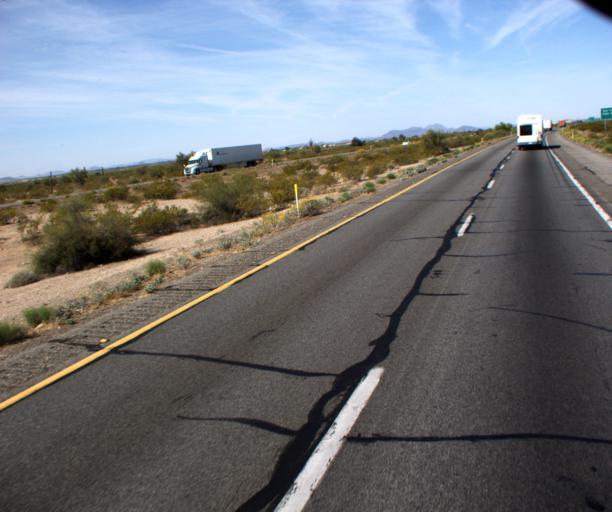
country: US
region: Arizona
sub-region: Maricopa County
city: Buckeye
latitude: 33.4346
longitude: -112.6550
